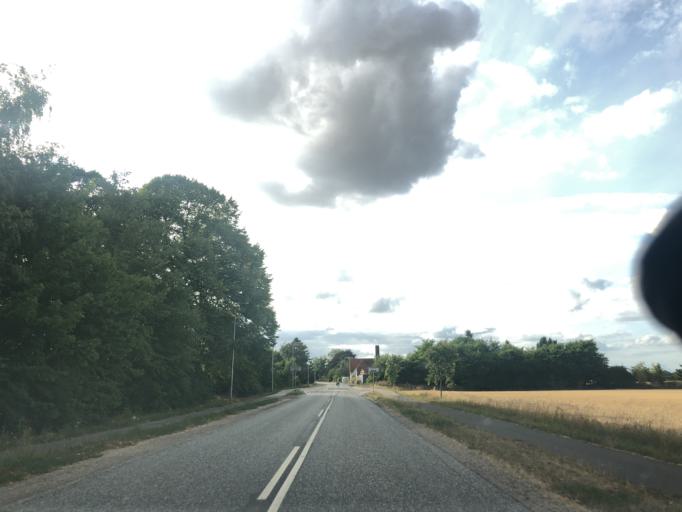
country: DK
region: Zealand
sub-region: Koge Kommune
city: Bjaeverskov
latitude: 55.4253
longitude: 11.9958
